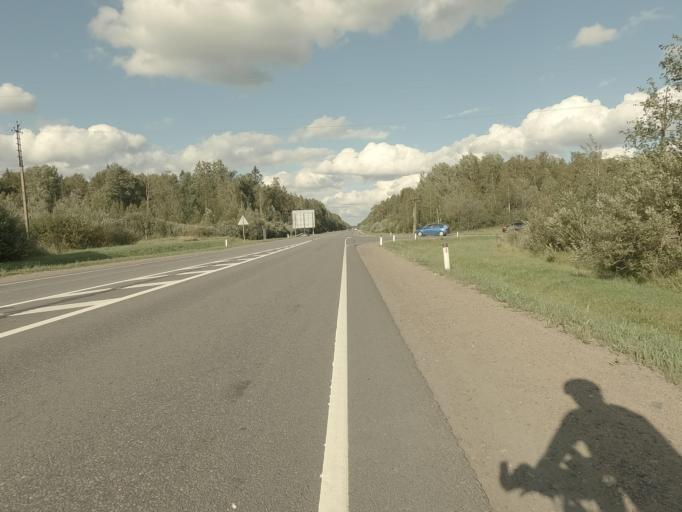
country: RU
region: Leningrad
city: Ul'yanovka
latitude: 59.6471
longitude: 30.8440
